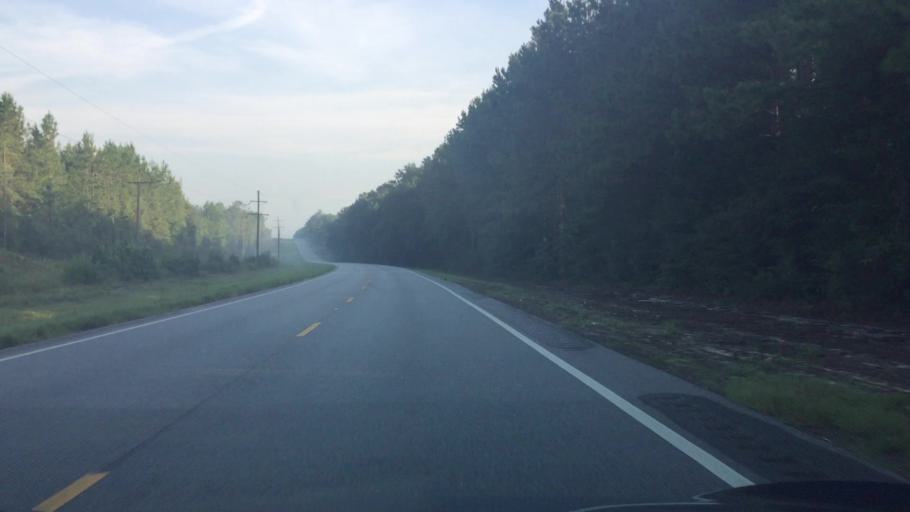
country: US
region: Alabama
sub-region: Covington County
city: Florala
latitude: 31.0577
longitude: -86.3921
